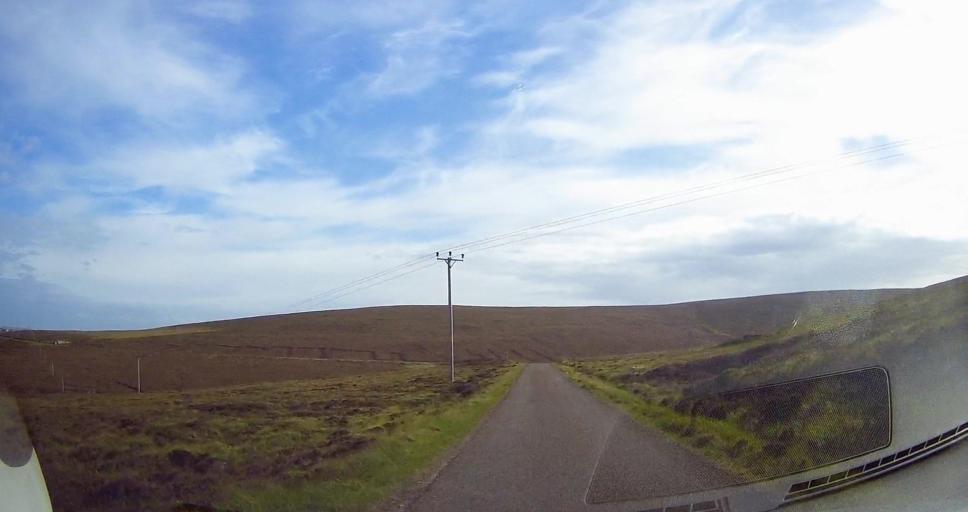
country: GB
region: Scotland
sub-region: Orkney Islands
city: Stromness
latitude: 58.8635
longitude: -3.2218
